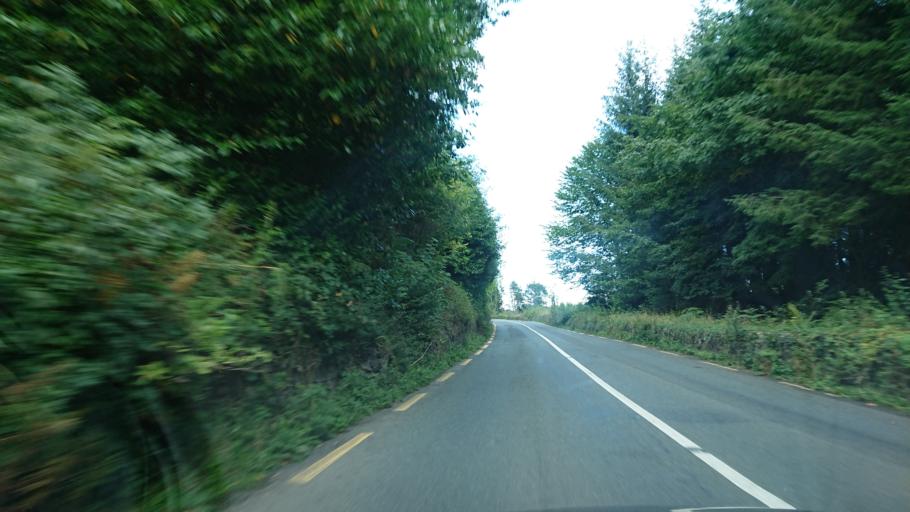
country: IE
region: Munster
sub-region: Waterford
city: Dungarvan
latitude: 52.1247
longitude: -7.6917
